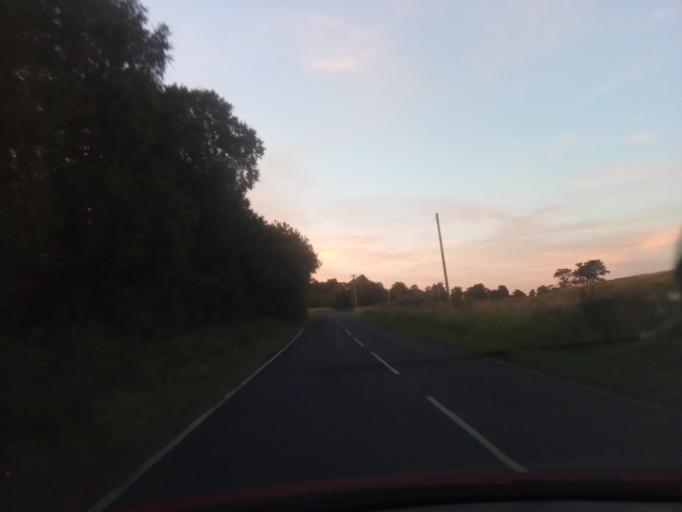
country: GB
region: England
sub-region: Northumberland
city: Bardon Mill
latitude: 54.9436
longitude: -2.2860
